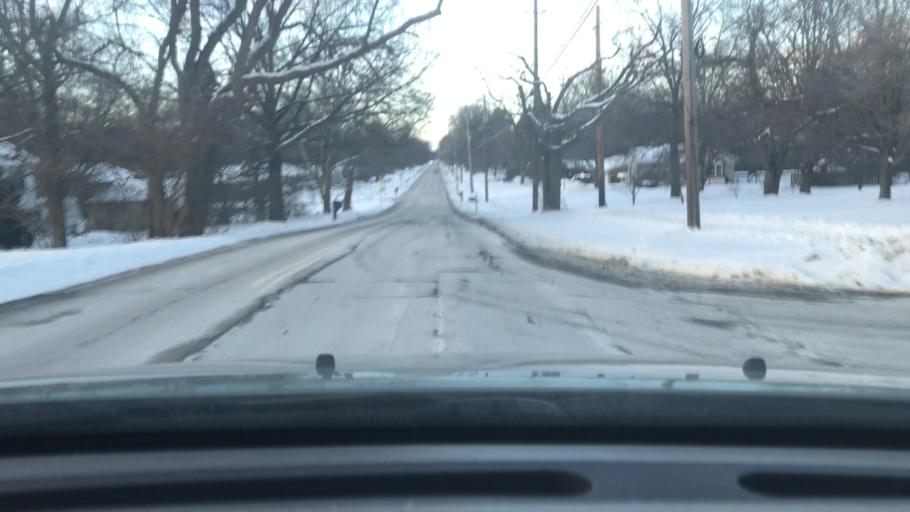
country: US
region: Ohio
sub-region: Lake County
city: Mentor
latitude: 41.6663
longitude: -81.3159
